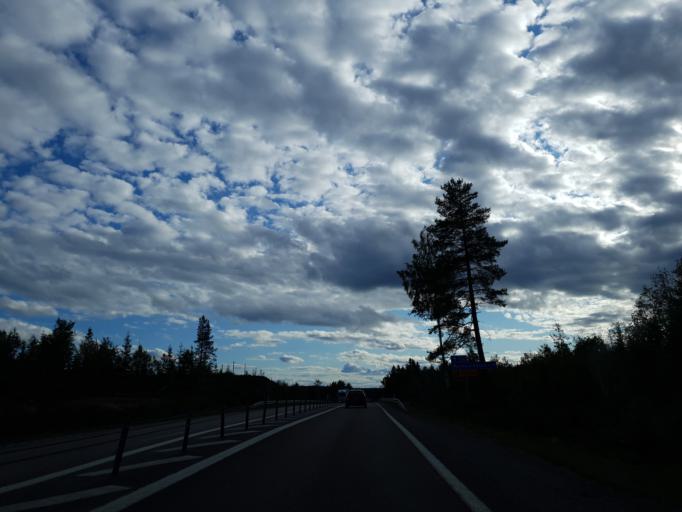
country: SE
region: Vaesternorrland
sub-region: Haernoesands Kommun
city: Haernoesand
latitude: 62.6020
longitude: 17.8141
